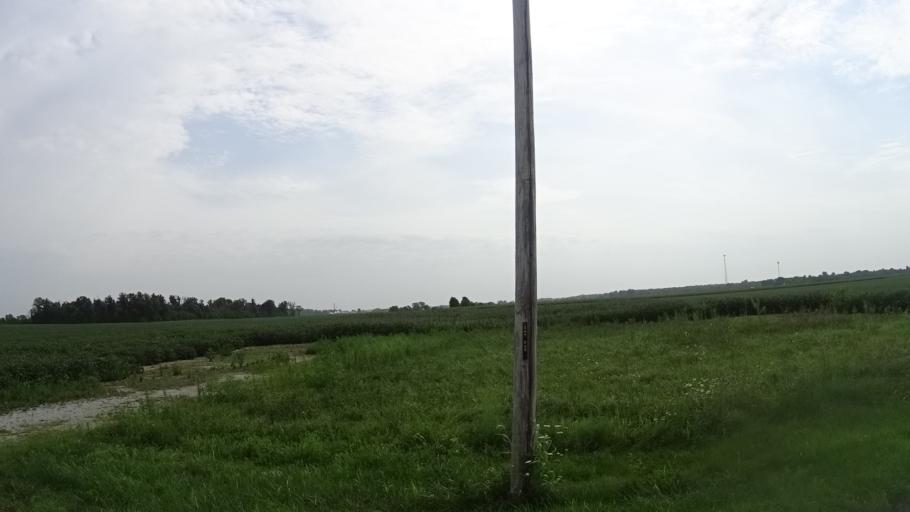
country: US
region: Indiana
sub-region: Madison County
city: Lapel
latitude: 40.0241
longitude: -85.8055
